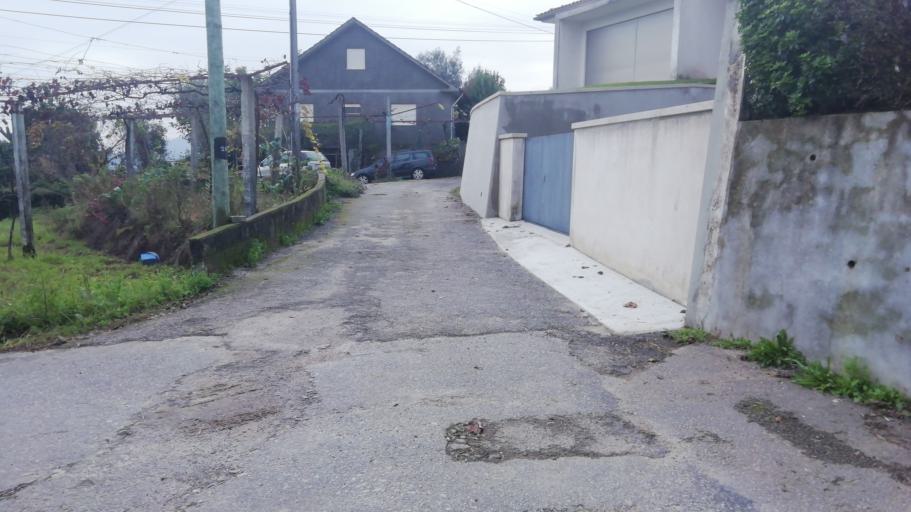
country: PT
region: Braga
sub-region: Vila Verde
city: Prado
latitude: 41.6533
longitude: -8.5107
